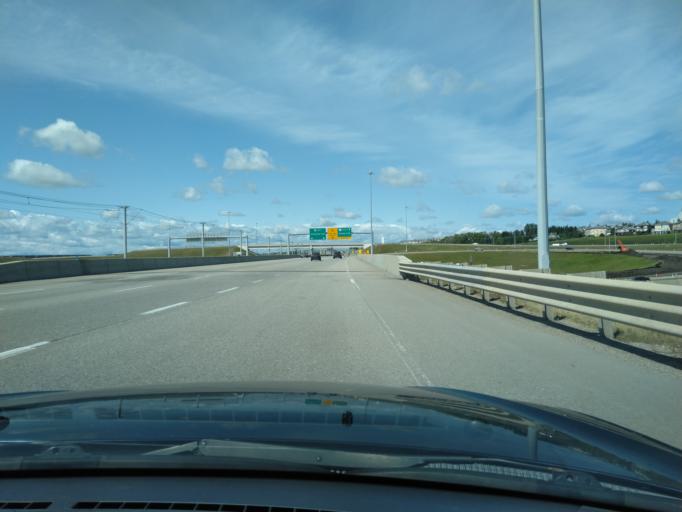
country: CA
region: Alberta
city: Calgary
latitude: 51.1309
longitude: -114.2262
